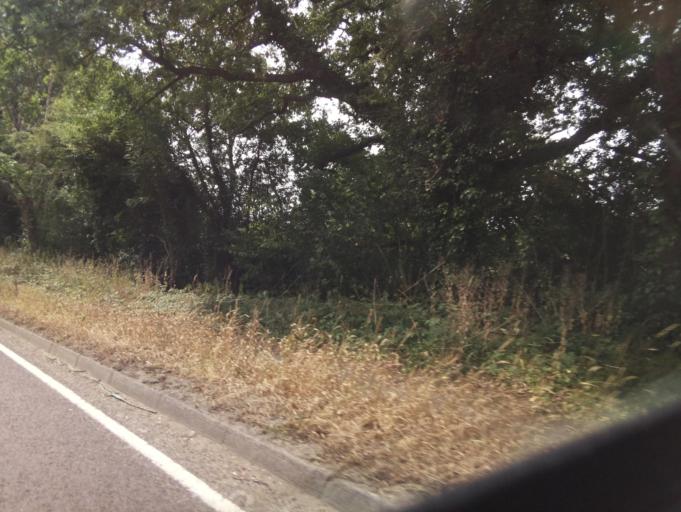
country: GB
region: England
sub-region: Surrey
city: Horley
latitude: 51.1751
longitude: -0.1941
